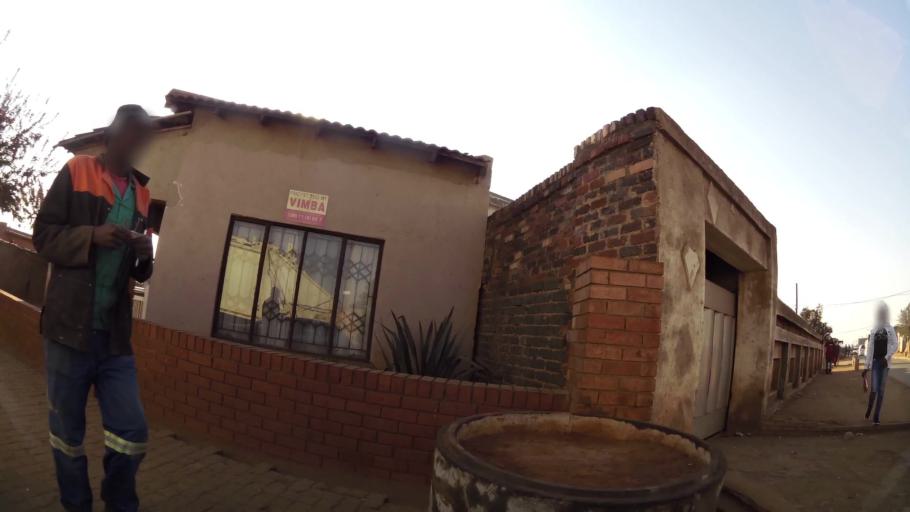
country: ZA
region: Gauteng
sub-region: Ekurhuleni Metropolitan Municipality
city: Tembisa
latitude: -25.9696
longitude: 28.2137
